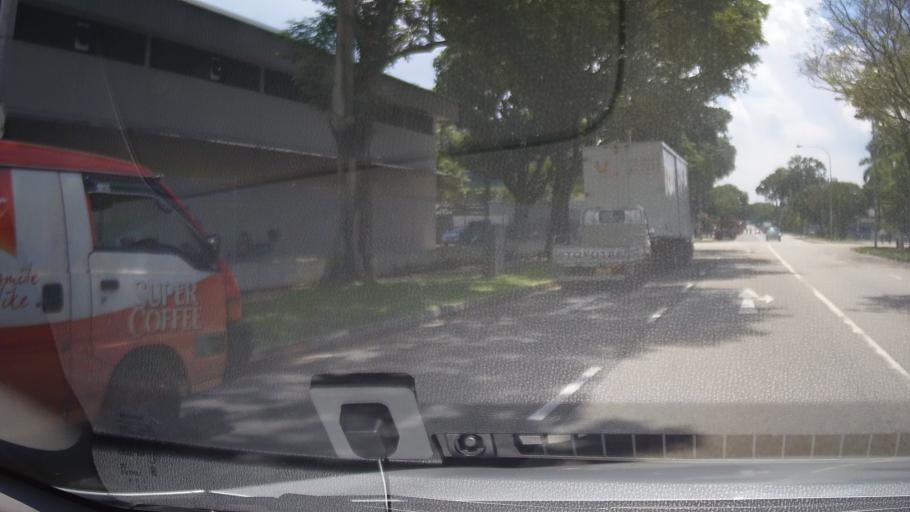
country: MY
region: Johor
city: Johor Bahru
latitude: 1.3313
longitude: 103.6938
